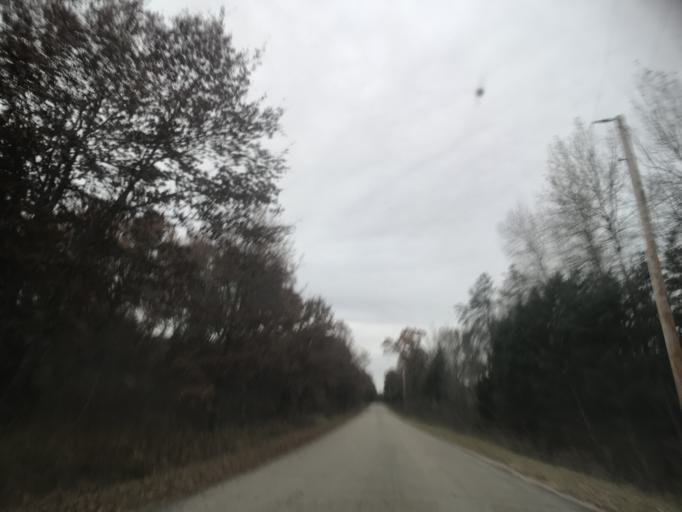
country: US
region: Wisconsin
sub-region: Oconto County
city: Gillett
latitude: 45.3128
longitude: -88.2763
